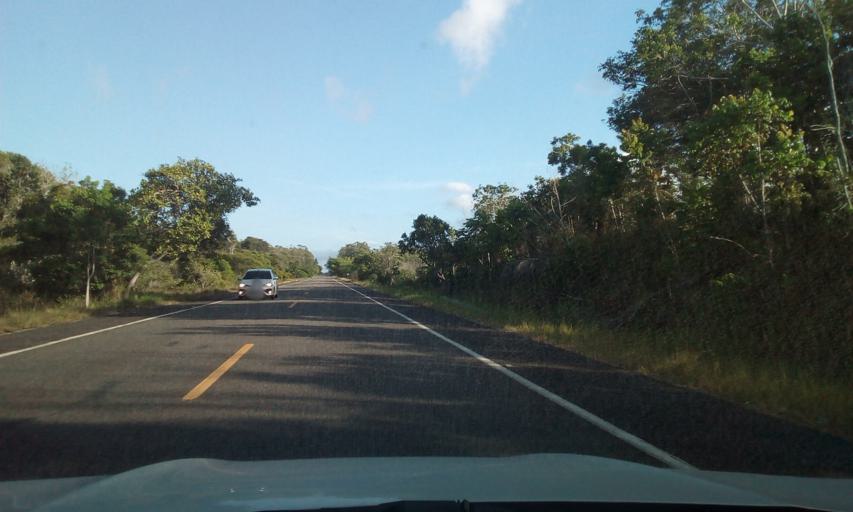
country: BR
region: Bahia
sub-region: Entre Rios
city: Entre Rios
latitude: -12.3290
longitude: -37.9043
